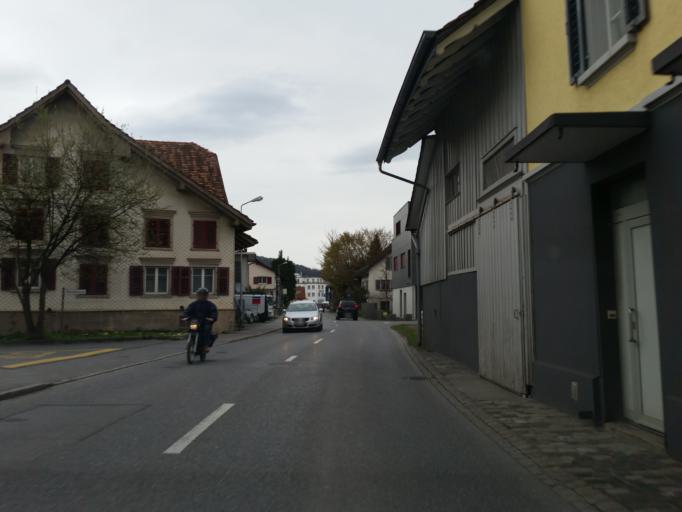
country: CH
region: Saint Gallen
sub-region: Wahlkreis Rheintal
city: Au
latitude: 47.4127
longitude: 9.6340
